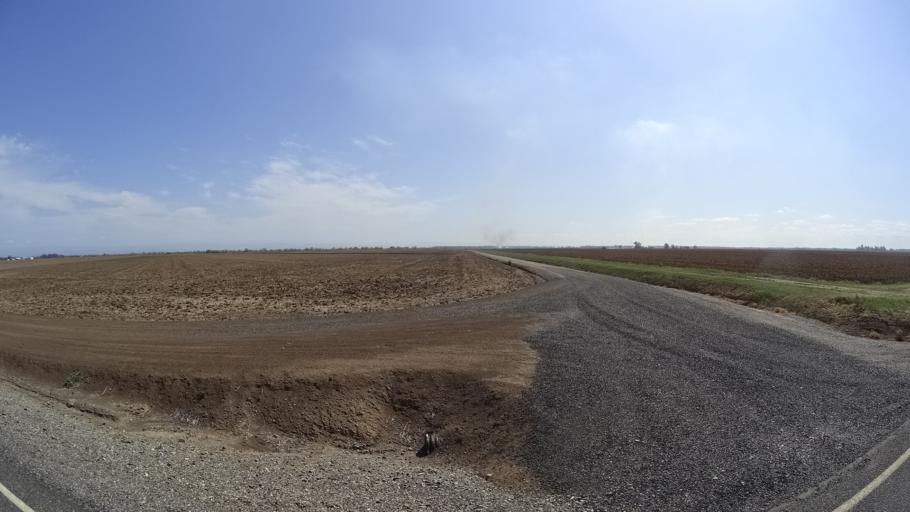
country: US
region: California
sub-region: Butte County
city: Durham
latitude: 39.5226
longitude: -121.9299
